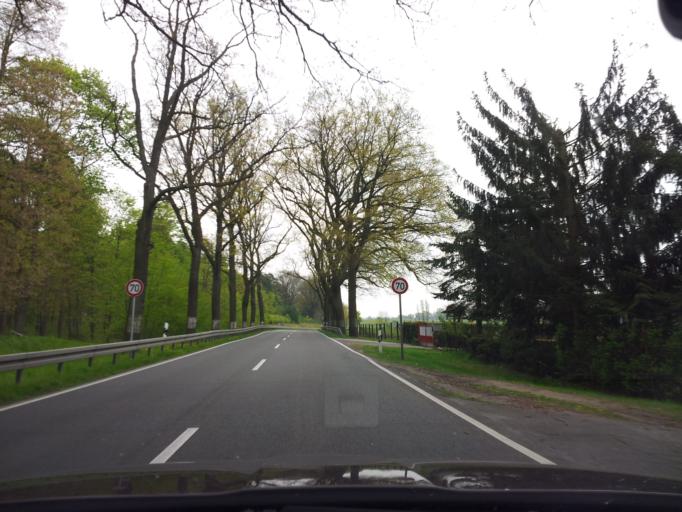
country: DE
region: Brandenburg
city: Muncheberg
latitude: 52.4996
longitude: 14.1019
